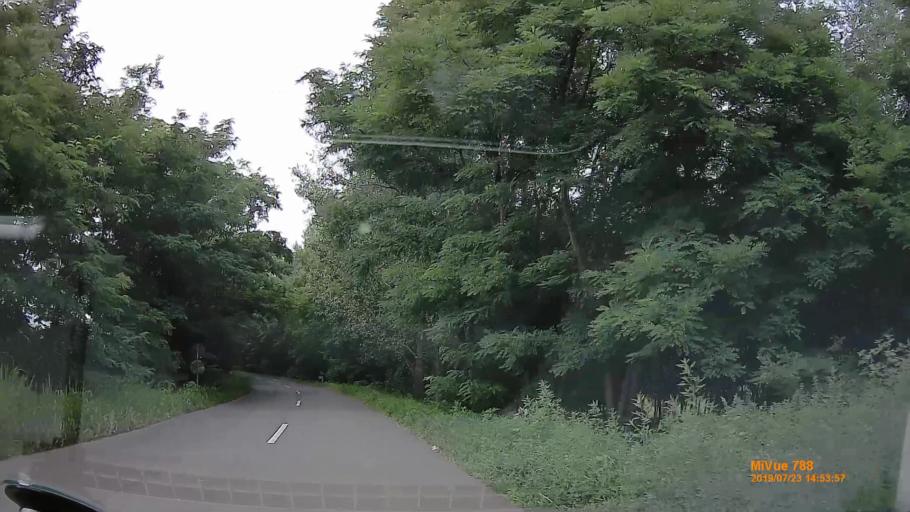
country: HU
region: Szabolcs-Szatmar-Bereg
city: Kalmanhaza
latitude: 47.8821
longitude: 21.6527
